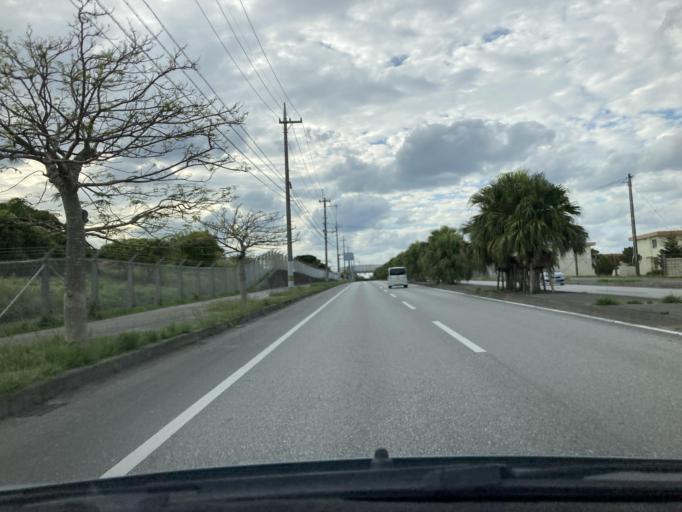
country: JP
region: Okinawa
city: Okinawa
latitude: 26.3602
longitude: 127.7985
